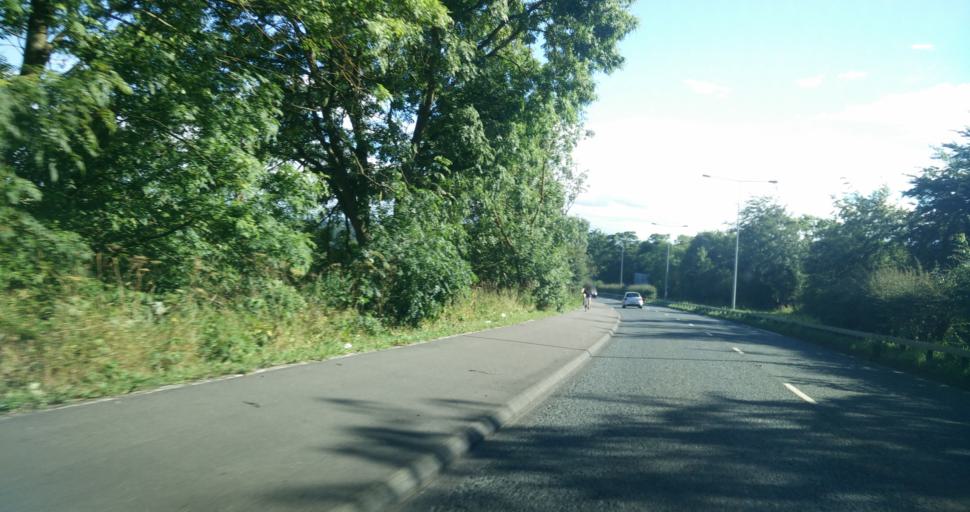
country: GB
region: England
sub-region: County Durham
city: Durham
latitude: 54.7502
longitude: -1.5906
